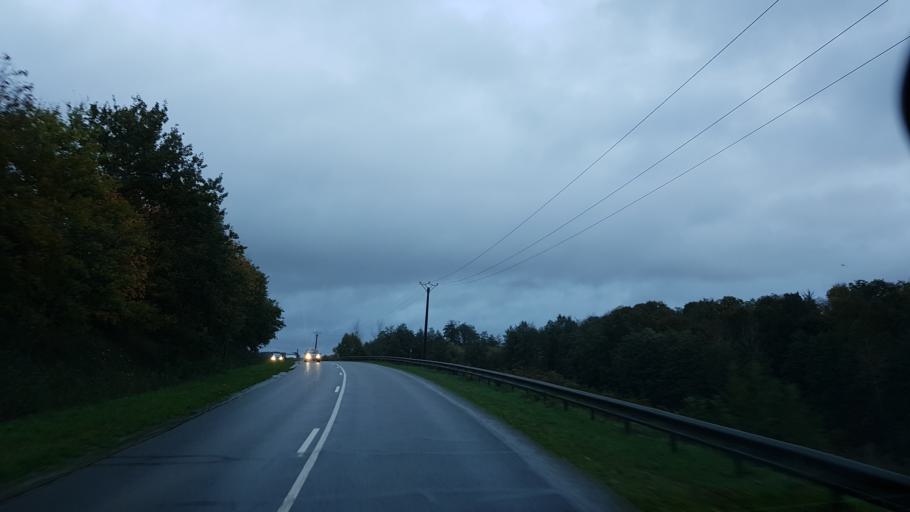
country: FR
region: Brittany
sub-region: Departement d'Ille-et-Vilaine
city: Balaze
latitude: 48.1398
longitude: -1.1739
